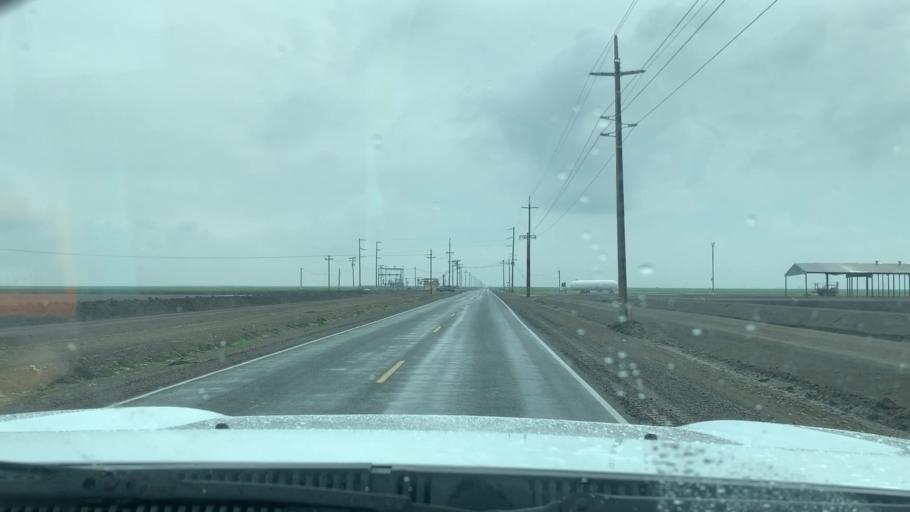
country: US
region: California
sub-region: Kings County
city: Corcoran
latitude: 35.9945
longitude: -119.5720
